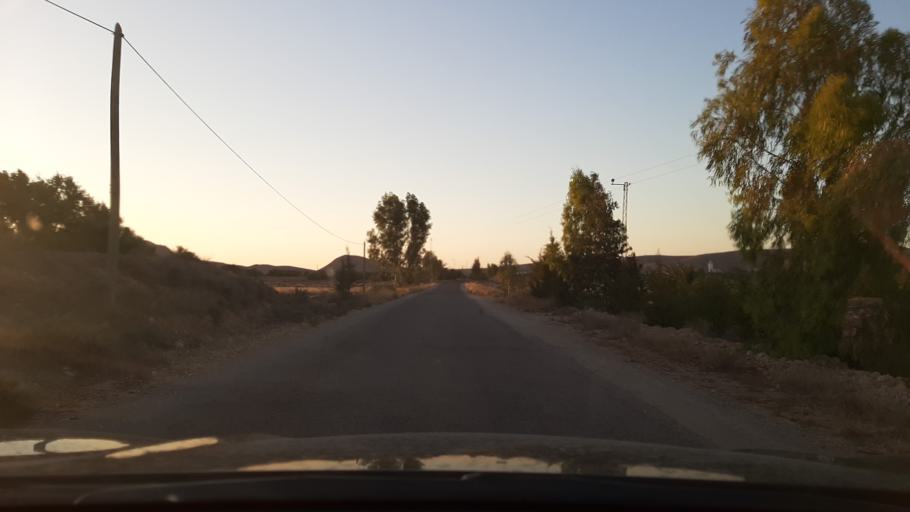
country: TN
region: Qabis
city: Matmata
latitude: 33.5631
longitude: 10.1805
